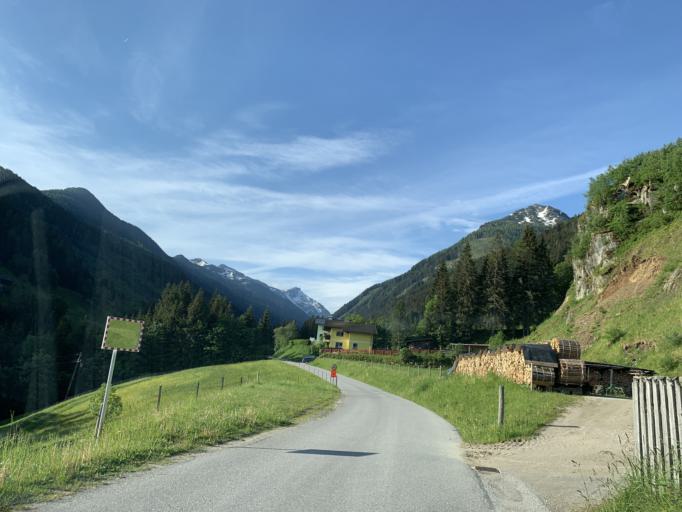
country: AT
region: Styria
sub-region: Politischer Bezirk Liezen
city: Schladming
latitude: 47.3740
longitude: 13.6140
